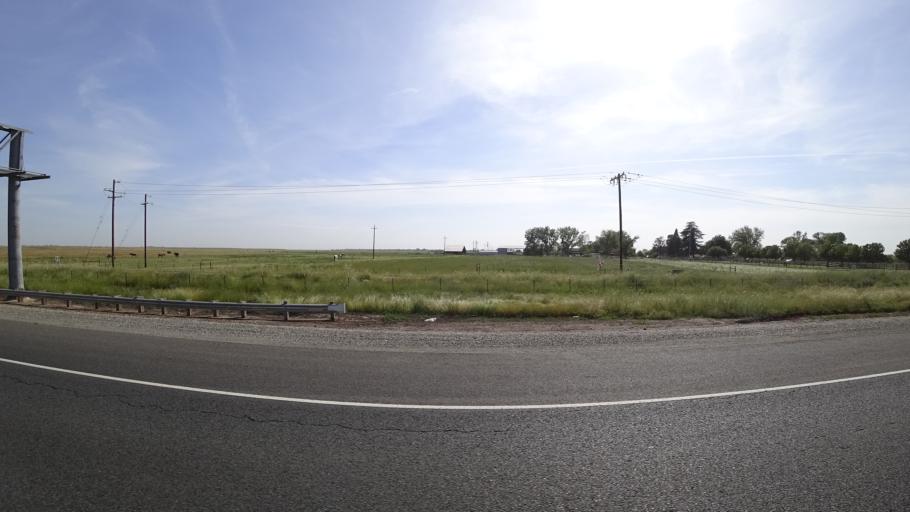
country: US
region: California
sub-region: Butte County
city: Durham
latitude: 39.6307
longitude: -121.7031
